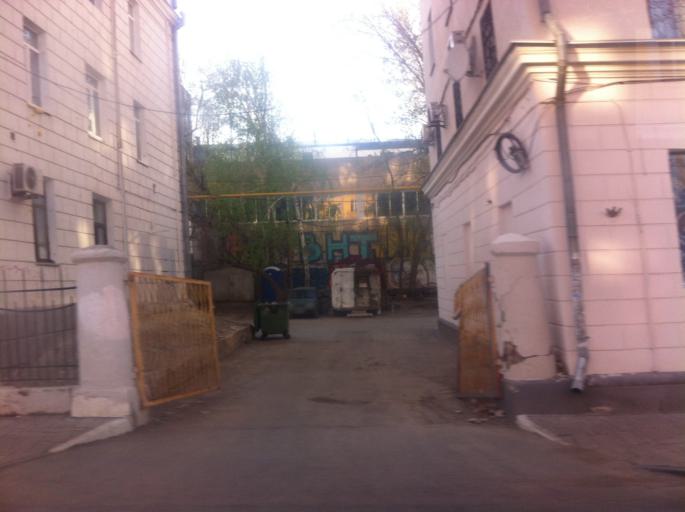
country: RU
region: Samara
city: Samara
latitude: 53.2027
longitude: 50.1143
